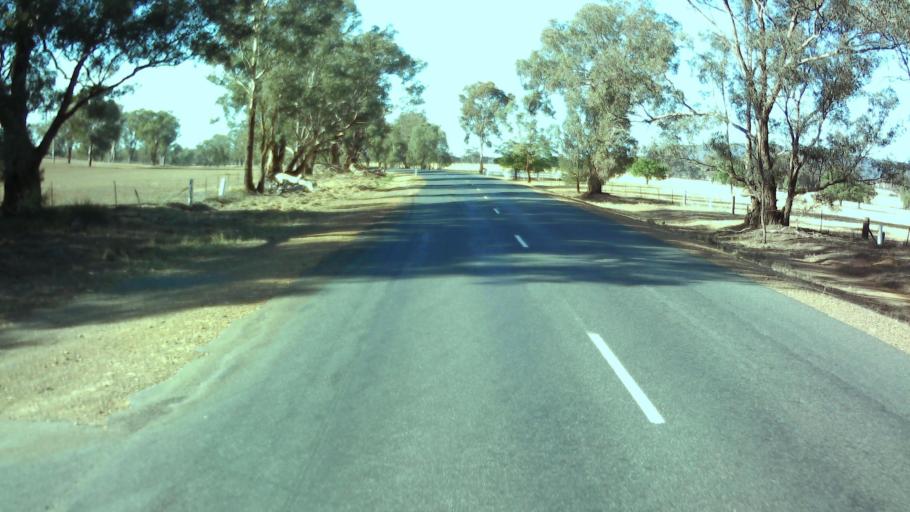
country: AU
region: New South Wales
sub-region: Weddin
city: Grenfell
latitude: -33.9419
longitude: 148.1360
